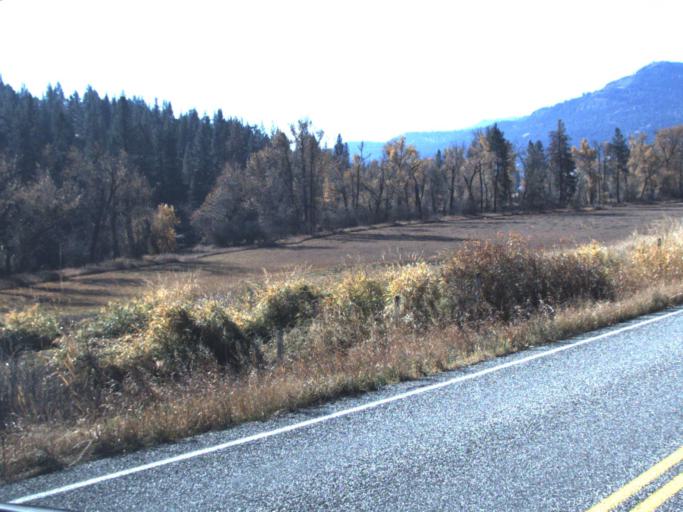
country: CA
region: British Columbia
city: Grand Forks
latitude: 48.8951
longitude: -118.5925
